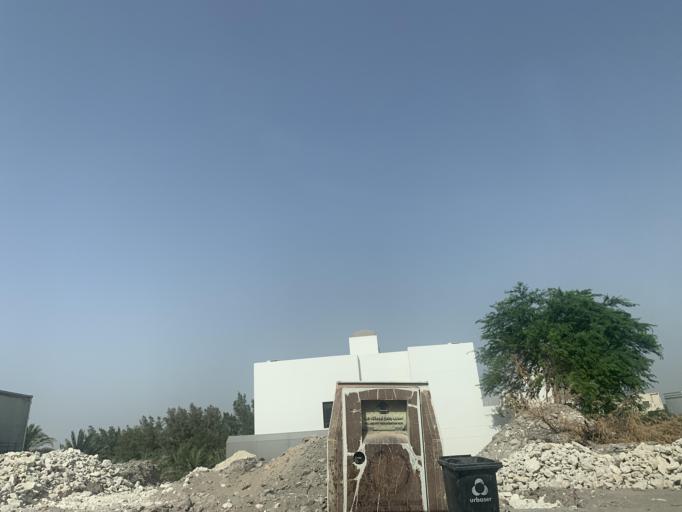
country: BH
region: Northern
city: Madinat `Isa
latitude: 26.1919
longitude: 50.4893
